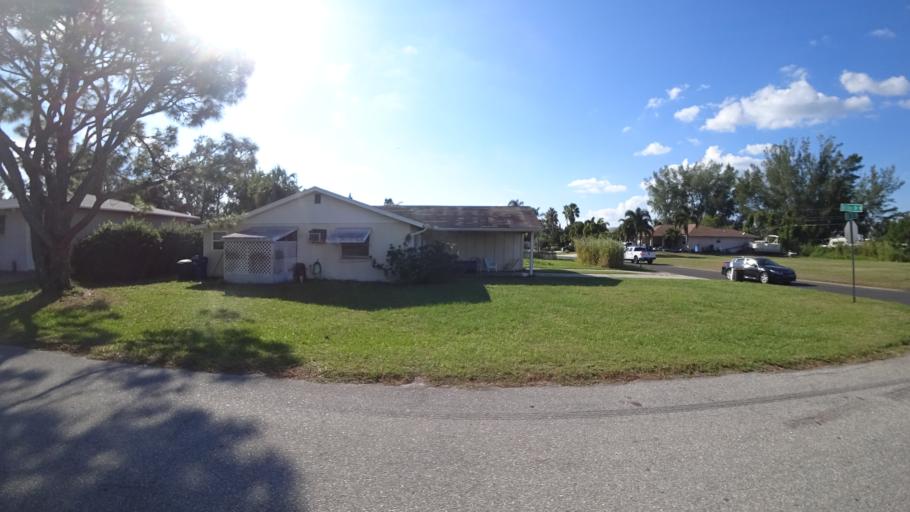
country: US
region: Florida
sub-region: Manatee County
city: Cortez
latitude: 27.4603
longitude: -82.6485
